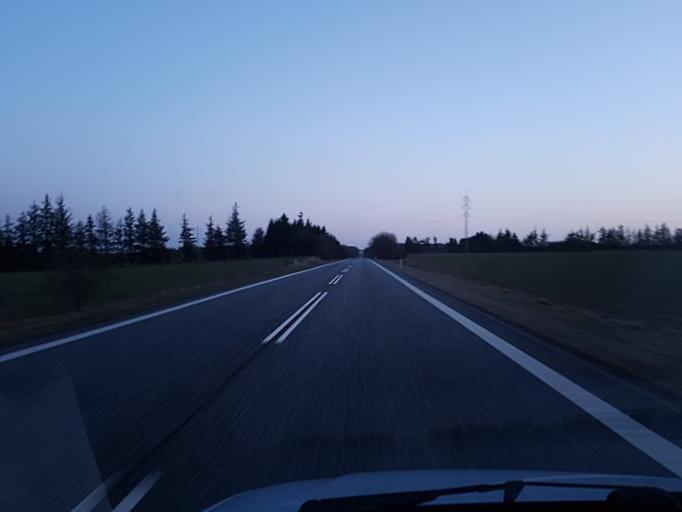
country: DK
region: Central Jutland
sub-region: Holstebro Kommune
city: Holstebro
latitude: 56.2382
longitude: 8.6076
